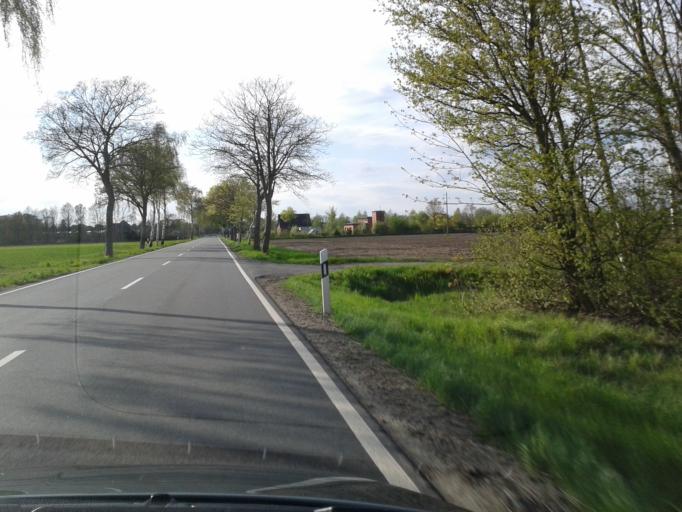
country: DE
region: Lower Saxony
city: Wustrow
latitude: 52.9201
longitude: 11.1413
